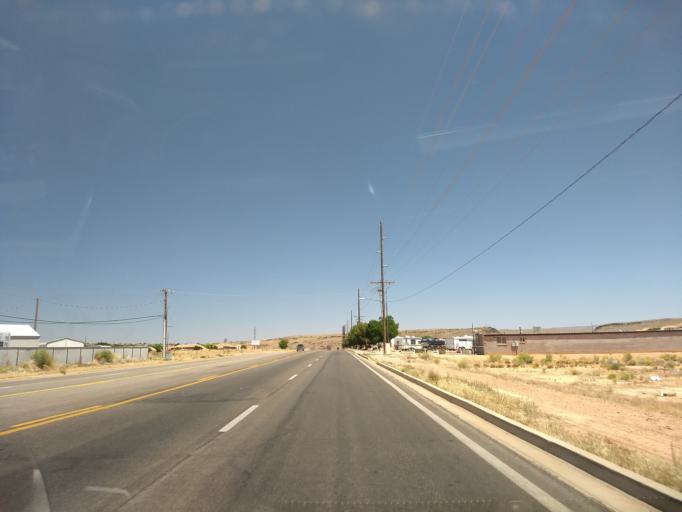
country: US
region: Utah
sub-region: Washington County
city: Washington
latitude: 37.1304
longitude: -113.4964
